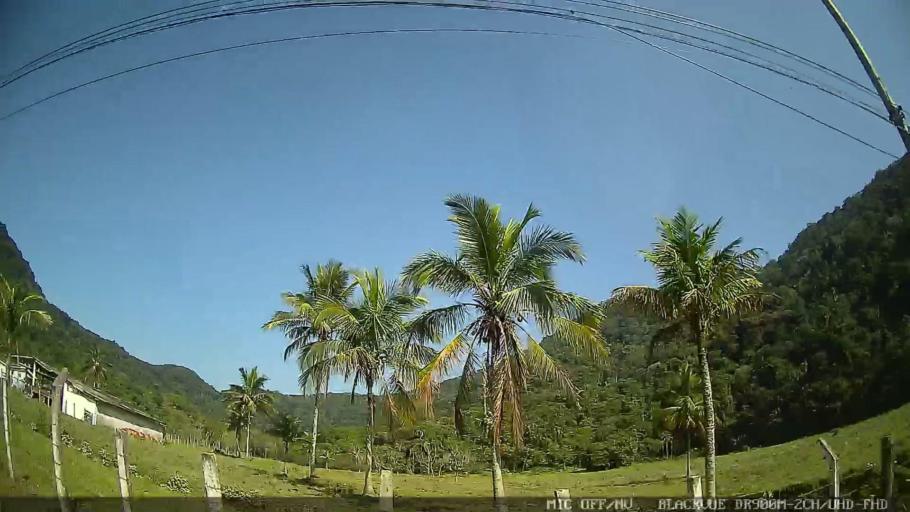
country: BR
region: Sao Paulo
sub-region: Guaruja
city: Guaruja
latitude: -24.0115
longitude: -46.3034
